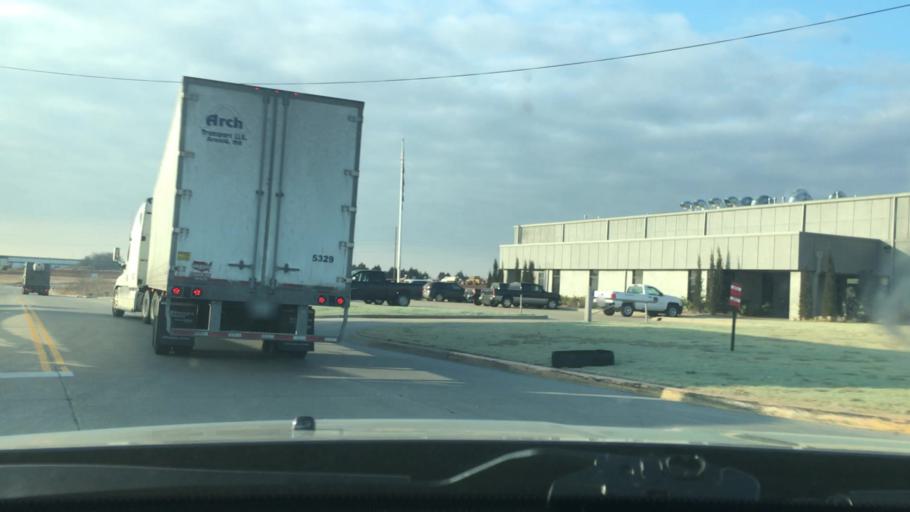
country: US
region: Oklahoma
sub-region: Carter County
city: Ardmore
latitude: 34.2019
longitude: -97.1685
